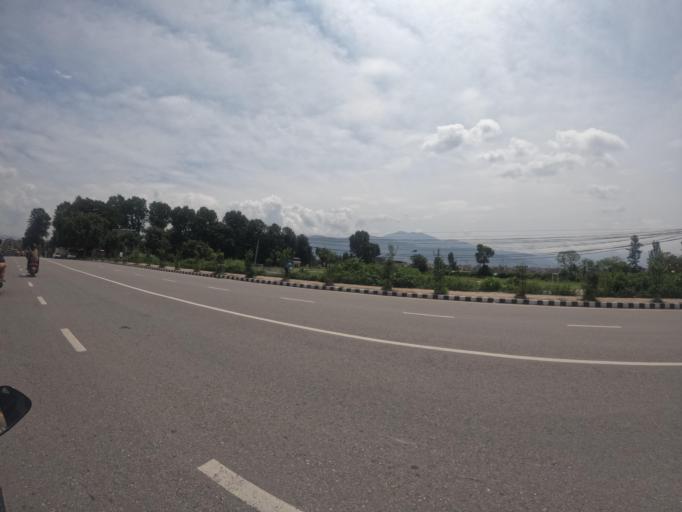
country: NP
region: Central Region
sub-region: Bagmati Zone
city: Bhaktapur
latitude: 27.6820
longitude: 85.3784
